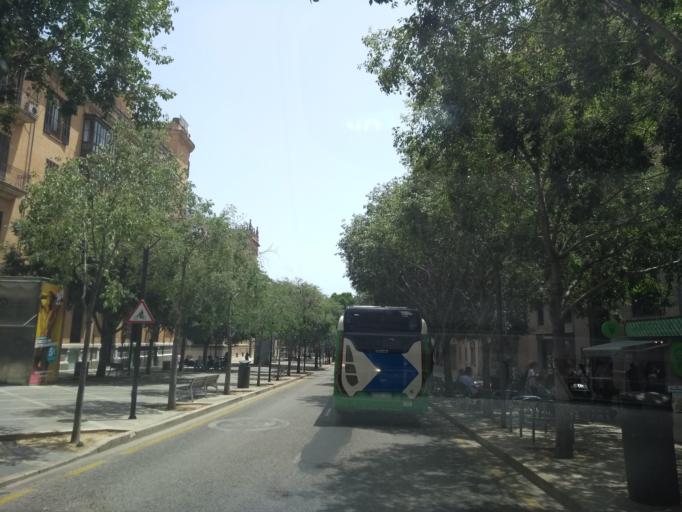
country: ES
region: Balearic Islands
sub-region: Illes Balears
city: Palma
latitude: 39.5762
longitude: 2.6467
